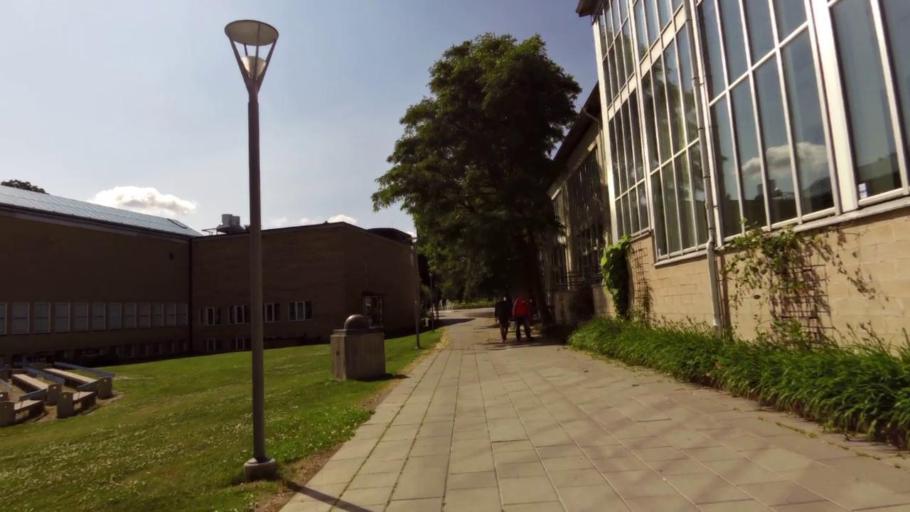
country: SE
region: OEstergoetland
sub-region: Linkopings Kommun
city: Linkoping
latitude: 58.4139
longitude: 15.6151
